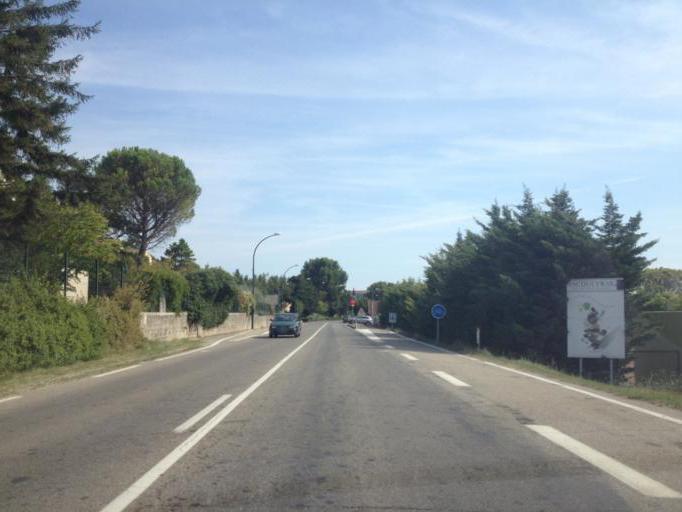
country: FR
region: Provence-Alpes-Cote d'Azur
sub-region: Departement du Vaucluse
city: Vacqueyras
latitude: 44.1438
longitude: 4.9862
